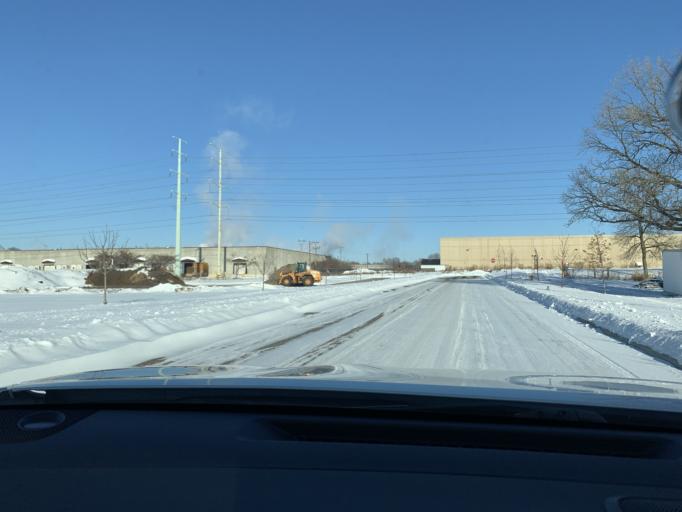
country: US
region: Minnesota
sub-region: Anoka County
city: Fridley
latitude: 45.0959
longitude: -93.2582
